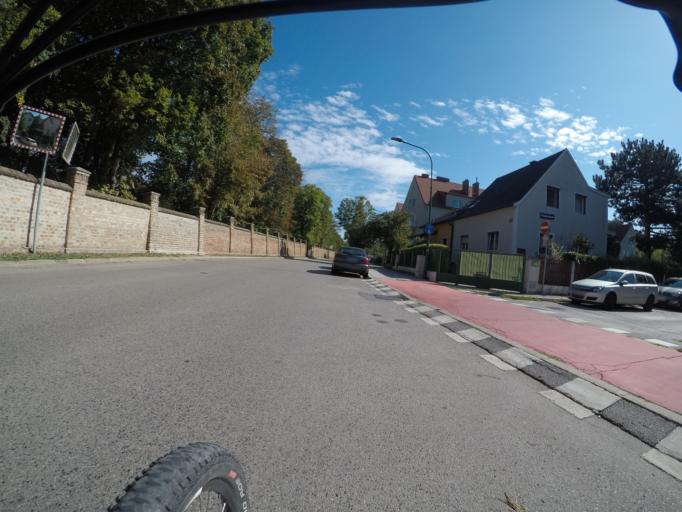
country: AT
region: Lower Austria
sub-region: Politischer Bezirk Modling
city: Modling
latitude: 48.0931
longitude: 16.2975
